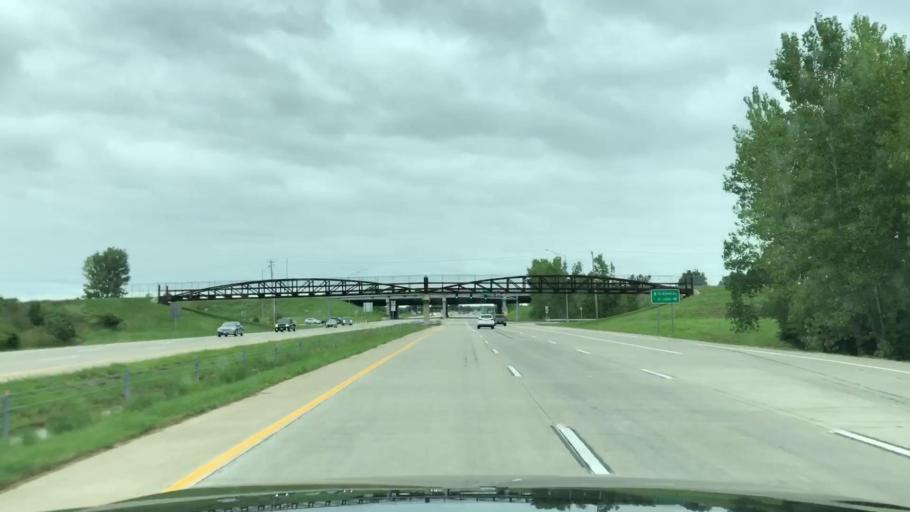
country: US
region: Missouri
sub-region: Saint Louis County
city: Maryland Heights
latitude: 38.7045
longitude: -90.5026
